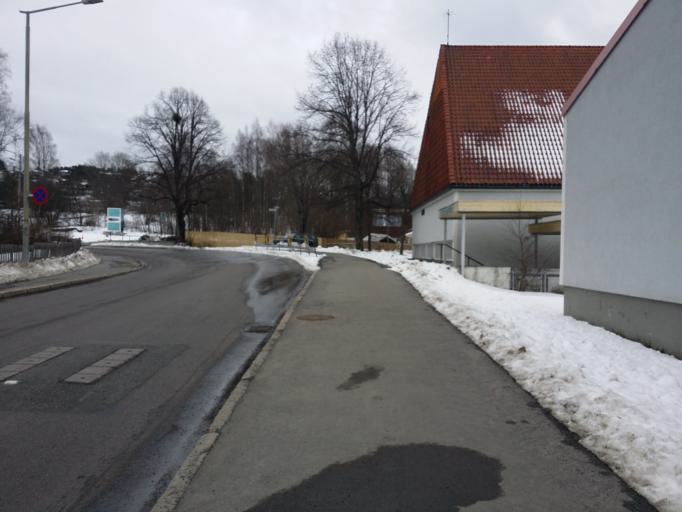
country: NO
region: Oslo
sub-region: Oslo
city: Oslo
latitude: 59.8955
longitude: 10.7851
